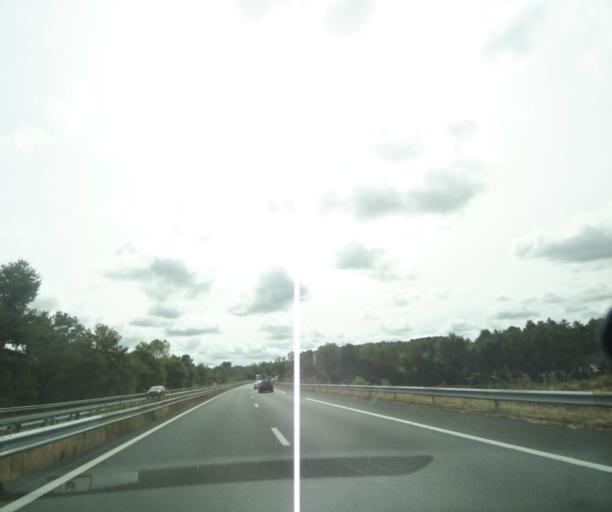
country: FR
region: Aquitaine
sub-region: Departement de la Gironde
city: Reignac
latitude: 45.2225
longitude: -0.5116
